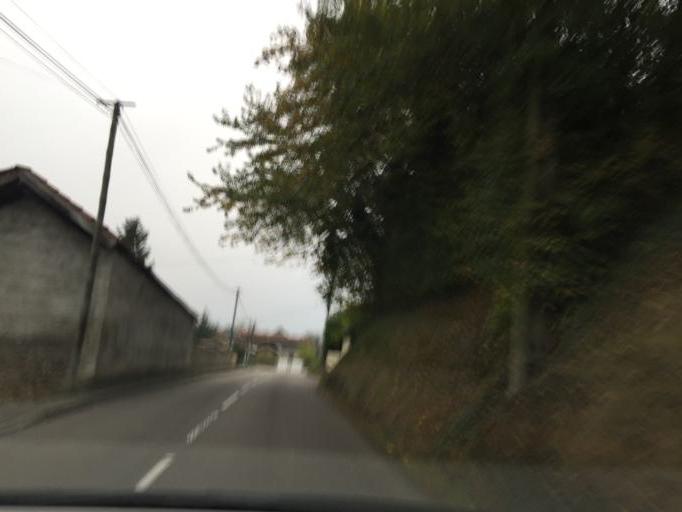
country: FR
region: Rhone-Alpes
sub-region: Departement de l'Isere
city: Clonas-sur-Vareze
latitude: 45.3958
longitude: 4.7891
